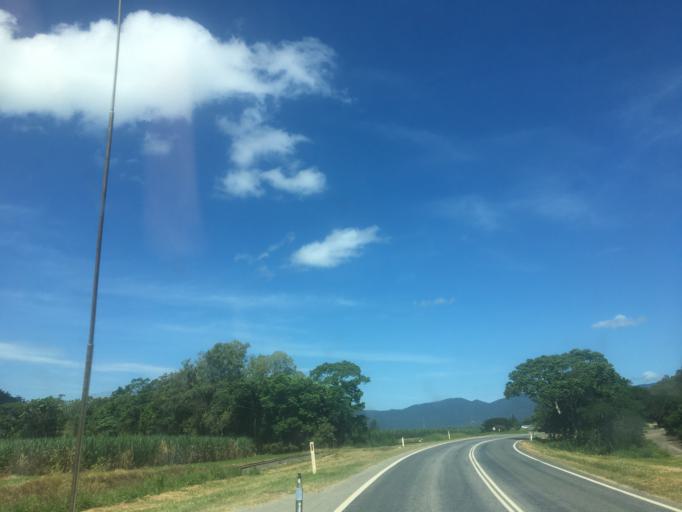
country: AU
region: Queensland
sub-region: Cairns
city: Woree
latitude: -17.0674
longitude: 145.7486
